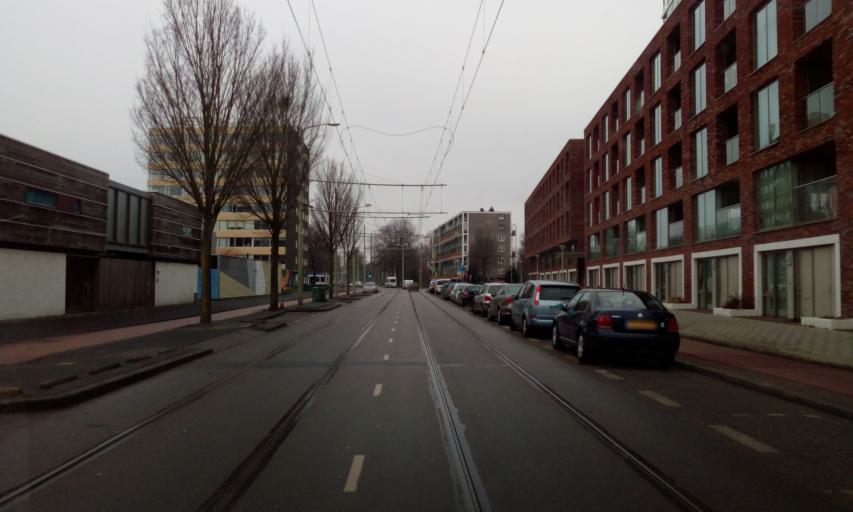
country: NL
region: South Holland
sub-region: Gemeente Westland
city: Kwintsheul
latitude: 52.0495
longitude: 4.2650
